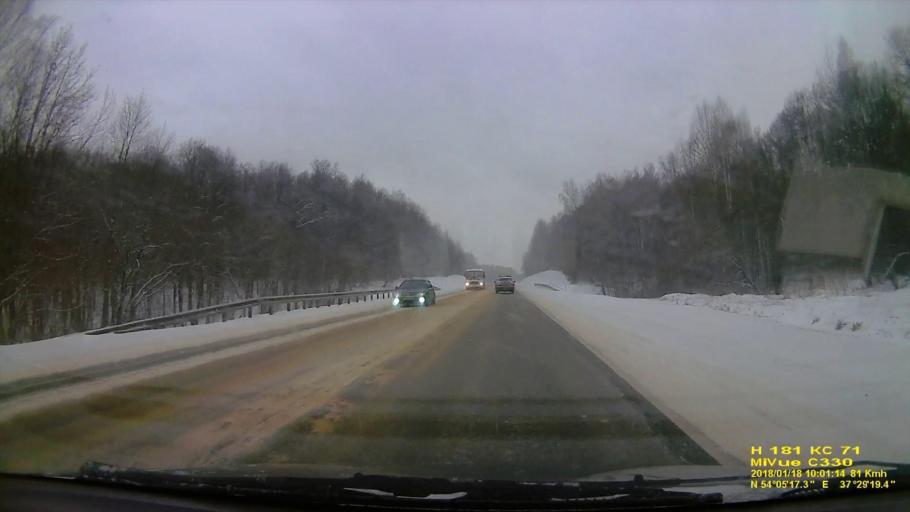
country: RU
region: Tula
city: Pervomayskiy
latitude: 54.0881
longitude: 37.4887
